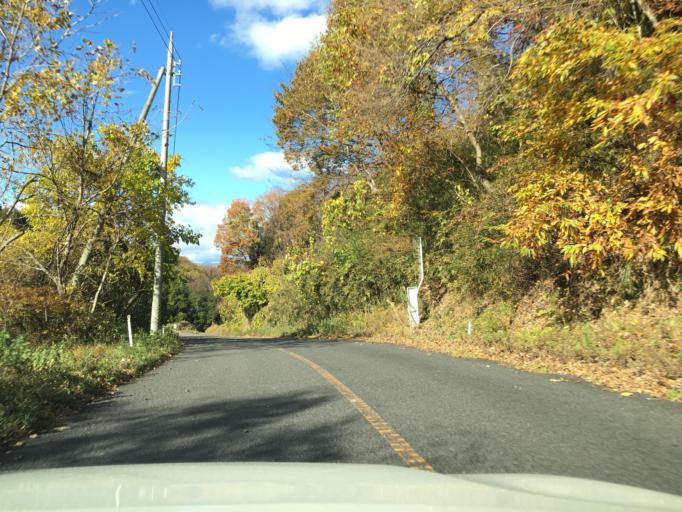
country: JP
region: Fukushima
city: Miharu
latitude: 37.4512
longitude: 140.5077
